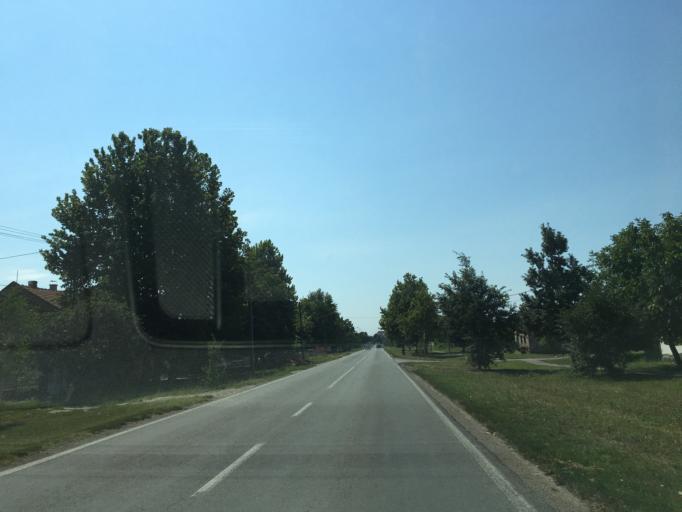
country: RS
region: Autonomna Pokrajina Vojvodina
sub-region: Juznobanatski Okrug
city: Pancevo
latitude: 44.8133
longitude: 20.6995
